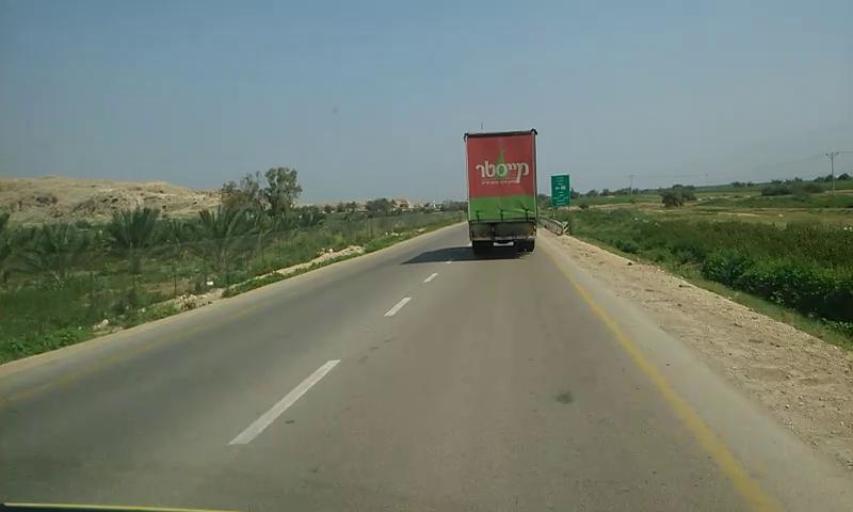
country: PS
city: Al Jiftlik
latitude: 32.1237
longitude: 35.5073
